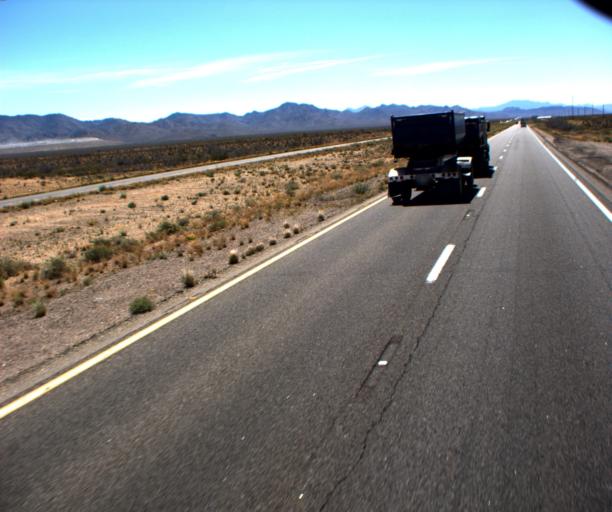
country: US
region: Arizona
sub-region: Mohave County
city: Golden Valley
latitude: 35.3519
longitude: -114.2270
